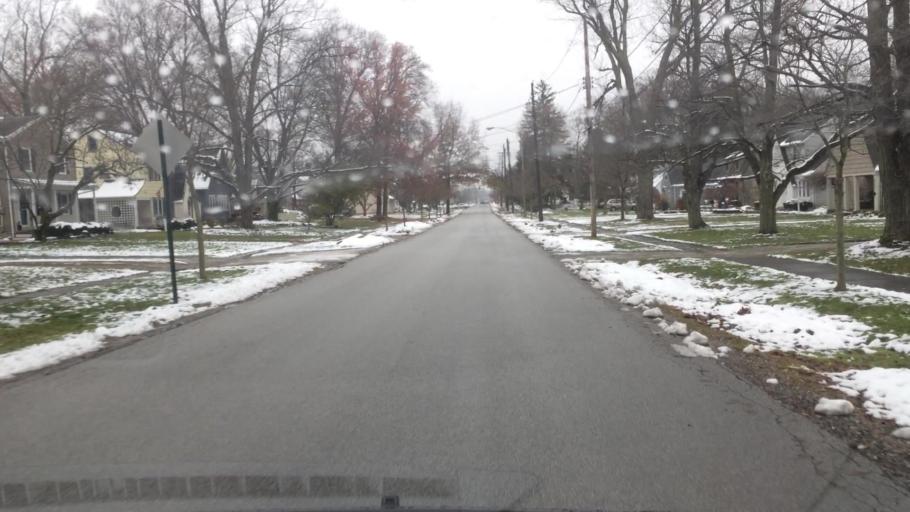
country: US
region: Ohio
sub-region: Cuyahoga County
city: Olmsted Falls
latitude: 41.3708
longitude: -81.9095
